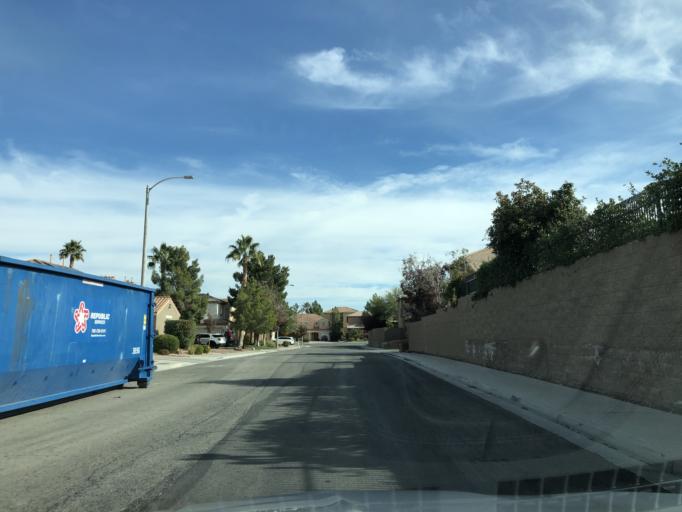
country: US
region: Nevada
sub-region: Clark County
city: Whitney
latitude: 36.0077
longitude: -115.0931
